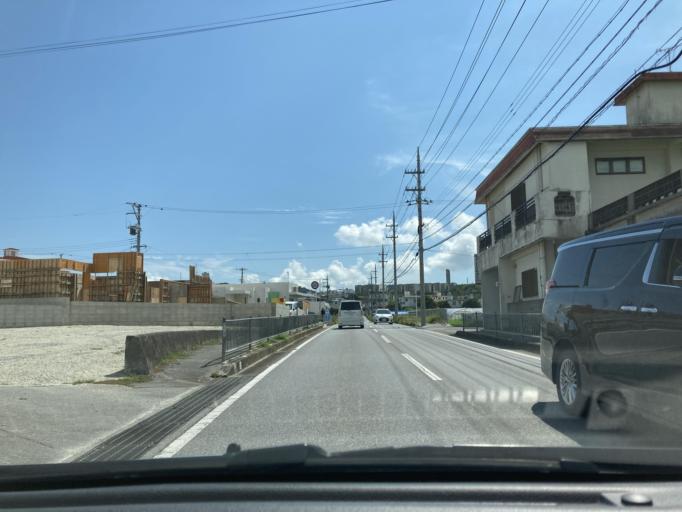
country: JP
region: Okinawa
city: Tomigusuku
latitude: 26.1820
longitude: 127.7391
